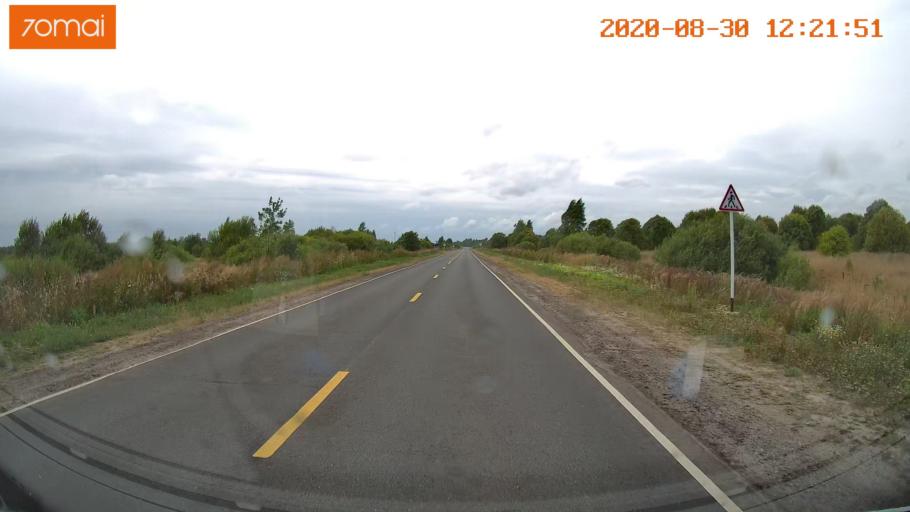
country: RU
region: Ivanovo
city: Yur'yevets
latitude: 57.3270
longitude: 42.8652
